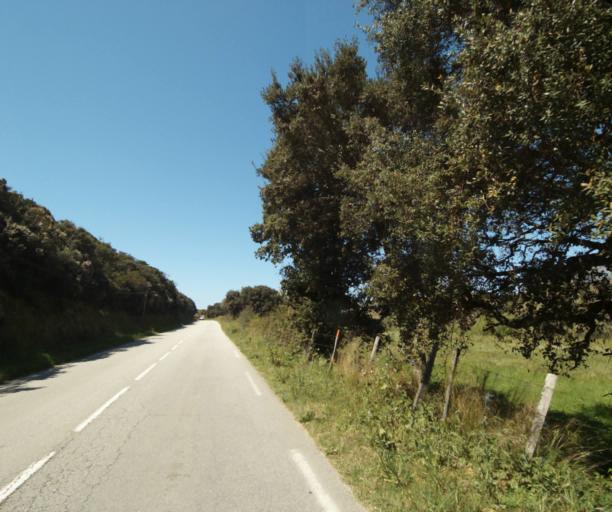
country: FR
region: Corsica
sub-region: Departement de la Corse-du-Sud
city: Propriano
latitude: 41.6592
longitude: 8.9125
